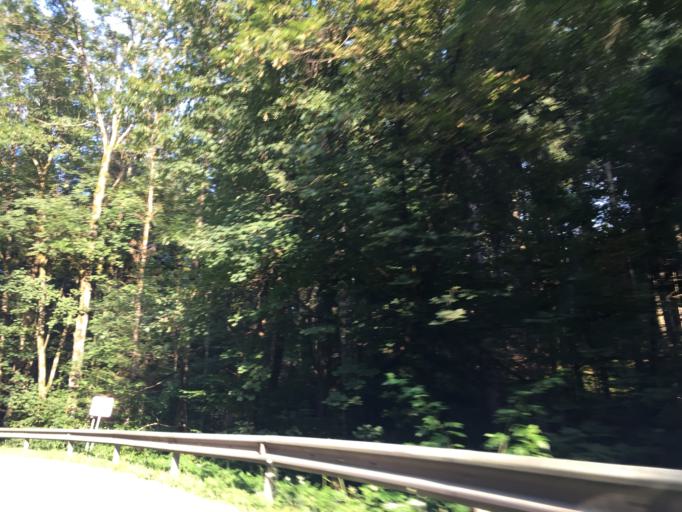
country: SI
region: Naklo
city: Naklo
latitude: 46.2966
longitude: 14.2672
